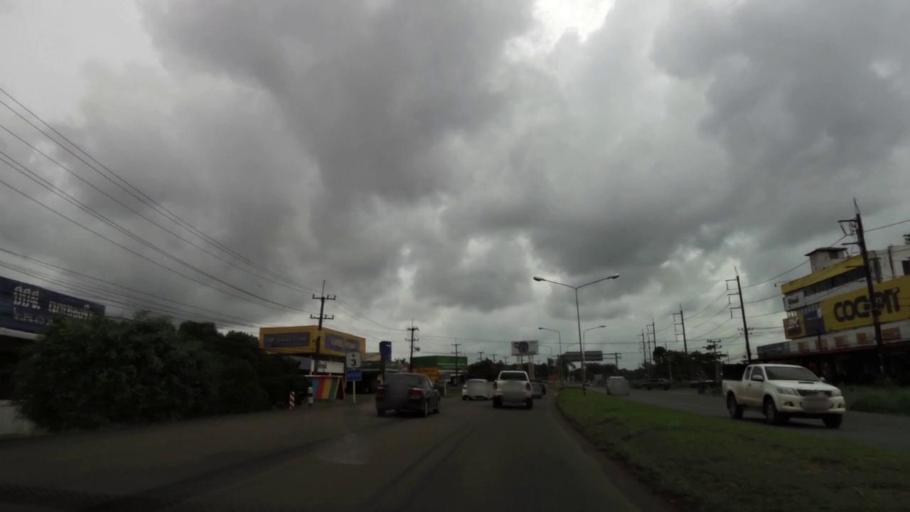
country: TH
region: Chanthaburi
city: Chanthaburi
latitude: 12.6036
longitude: 102.1347
